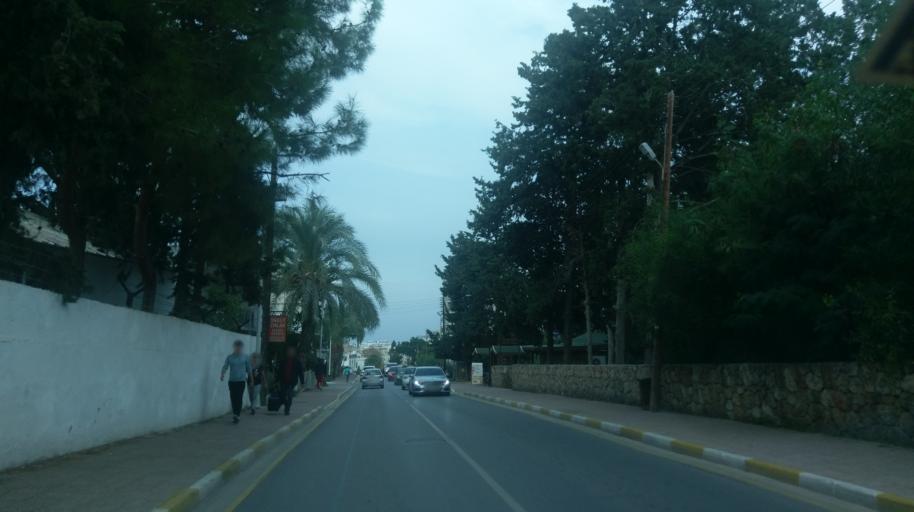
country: CY
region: Keryneia
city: Kyrenia
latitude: 35.3380
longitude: 33.3128
